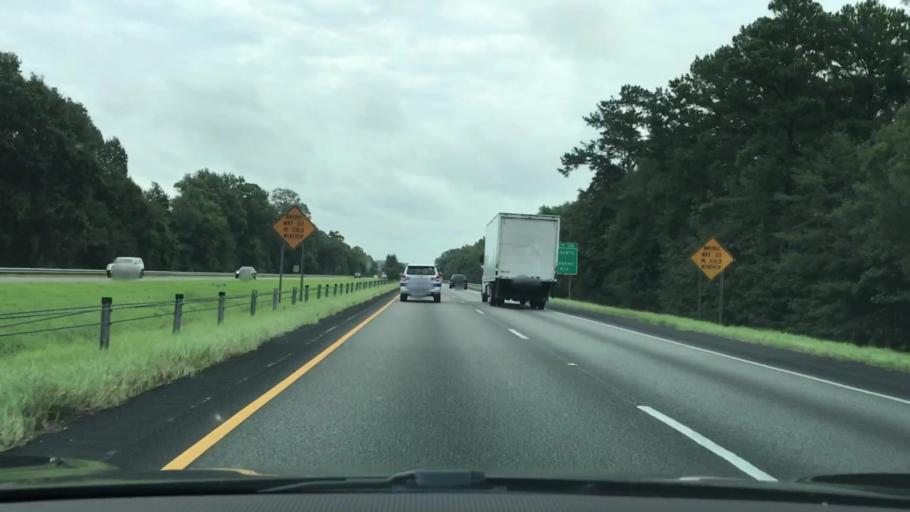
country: US
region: Alabama
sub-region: Elmore County
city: Tallassee
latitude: 32.4260
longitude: -85.9134
